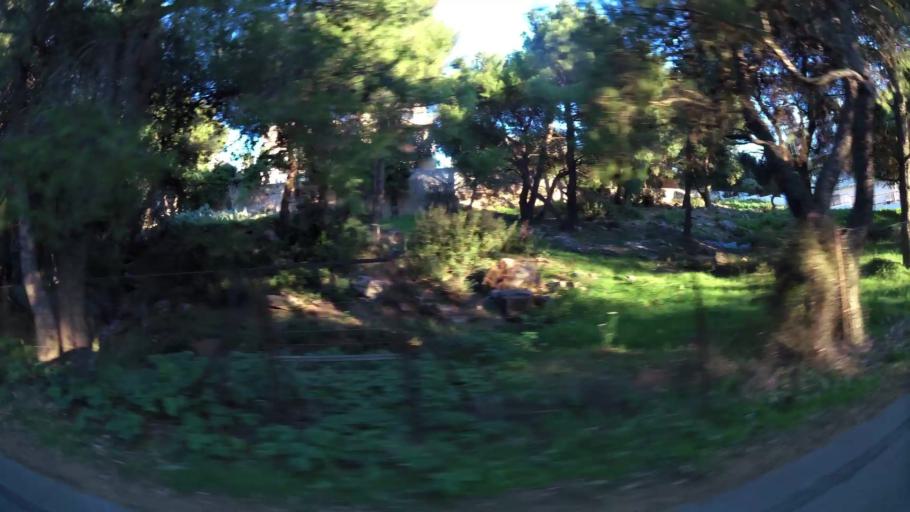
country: GR
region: Attica
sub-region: Nomarchia Athinas
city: Penteli
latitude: 38.0481
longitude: 23.8544
